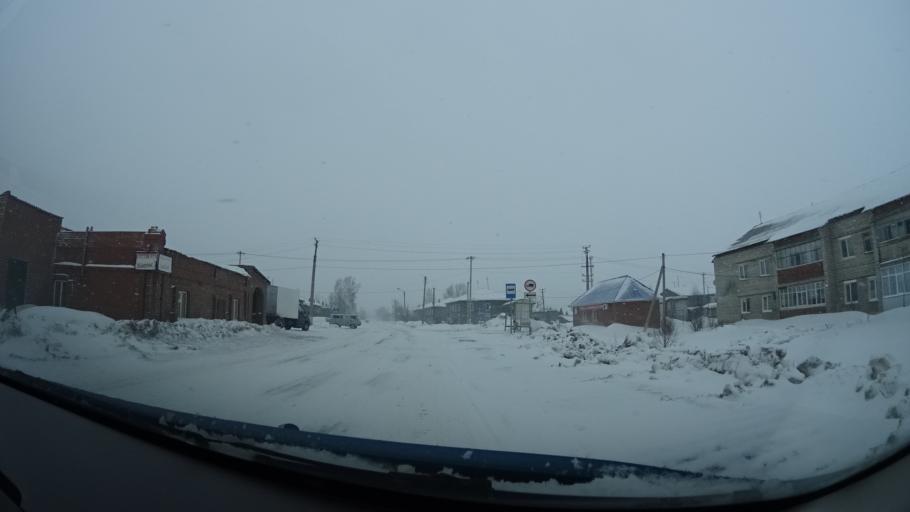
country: RU
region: Perm
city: Kuyeda
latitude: 56.4326
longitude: 55.5749
